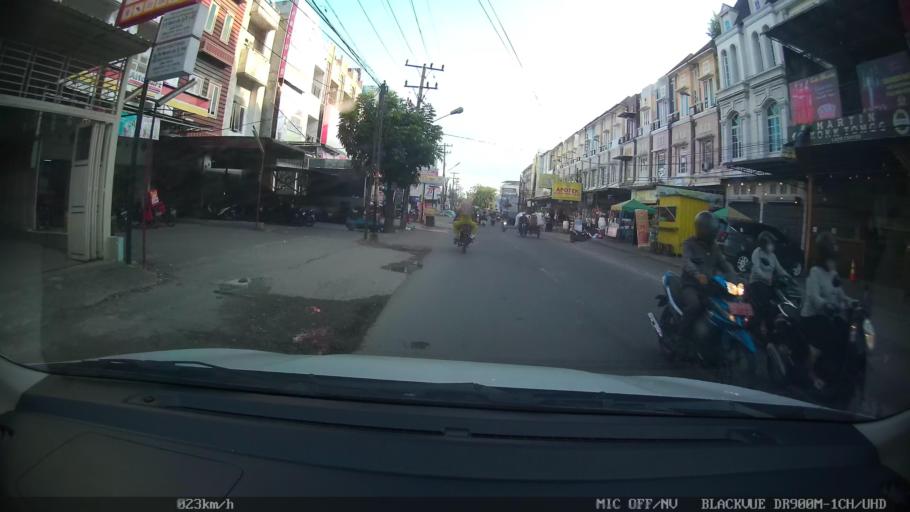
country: ID
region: North Sumatra
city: Medan
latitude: 3.6159
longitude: 98.6658
